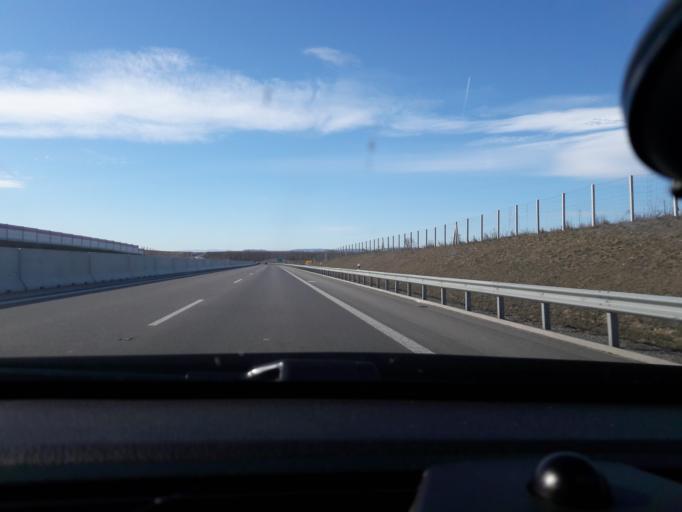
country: SK
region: Banskobystricky
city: Hrochot,Slovakia
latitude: 48.5712
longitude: 19.2719
